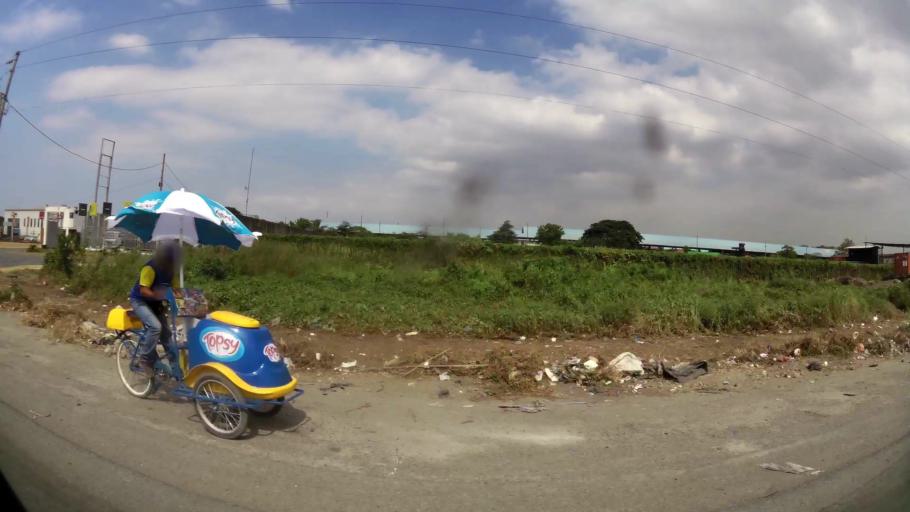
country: EC
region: Guayas
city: Santa Lucia
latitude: -2.0852
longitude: -79.9447
